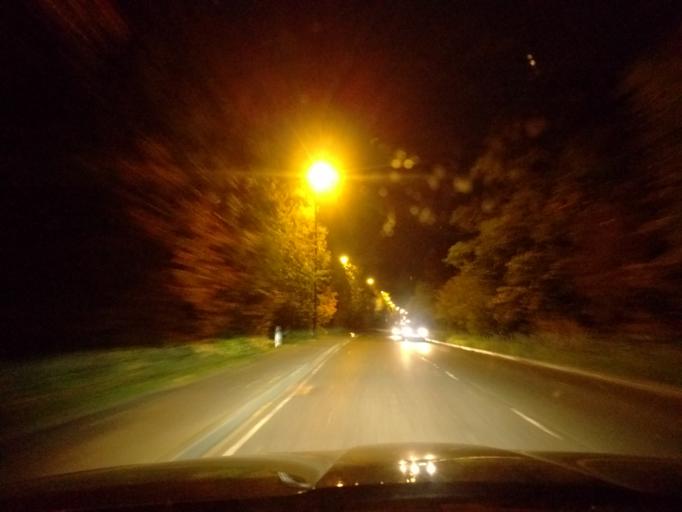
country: GB
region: England
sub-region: Northumberland
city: Backworth
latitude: 55.0187
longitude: -1.5426
